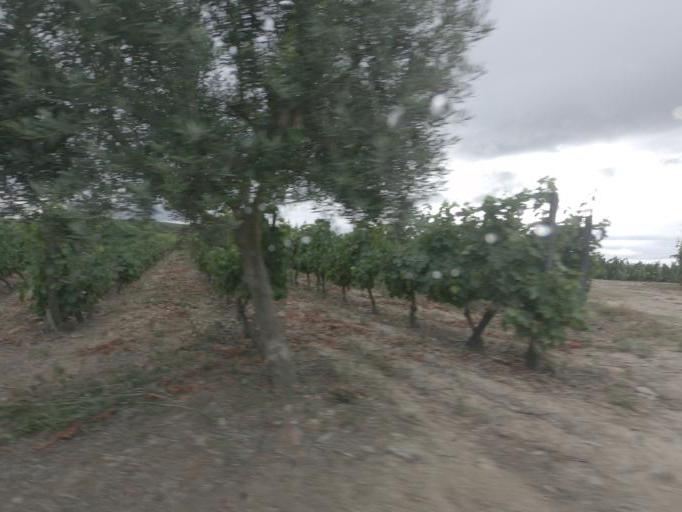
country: PT
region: Vila Real
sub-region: Sabrosa
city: Sabrosa
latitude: 41.2421
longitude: -7.4971
